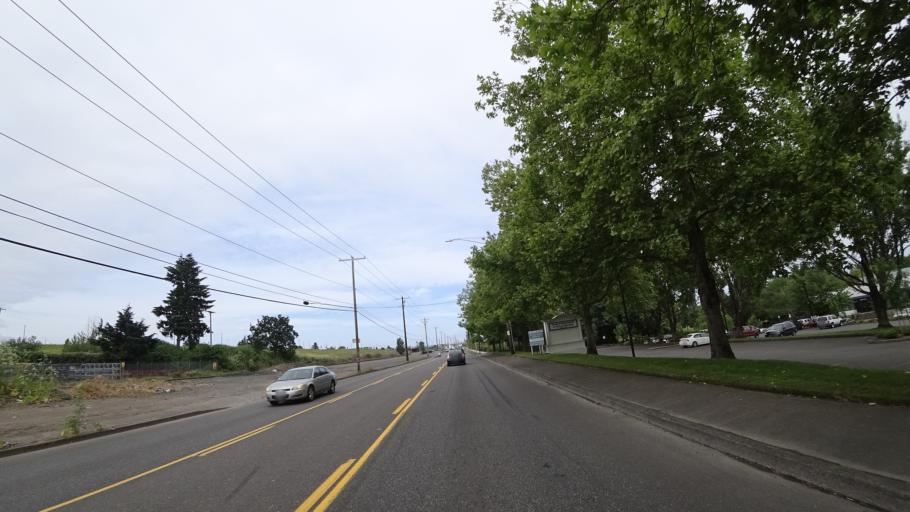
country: US
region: Oregon
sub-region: Multnomah County
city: Lents
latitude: 45.5656
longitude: -122.5826
